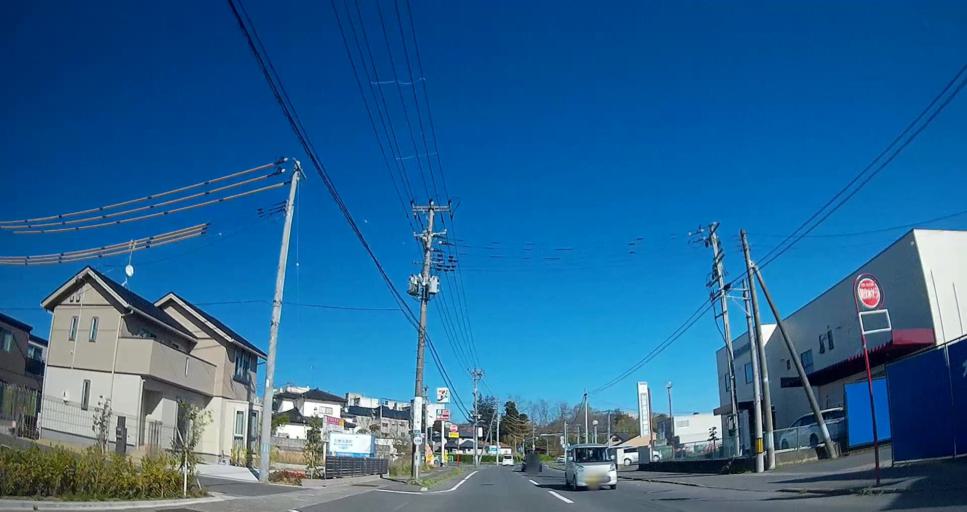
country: JP
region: Miyagi
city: Ishinomaki
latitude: 38.4252
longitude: 141.2917
